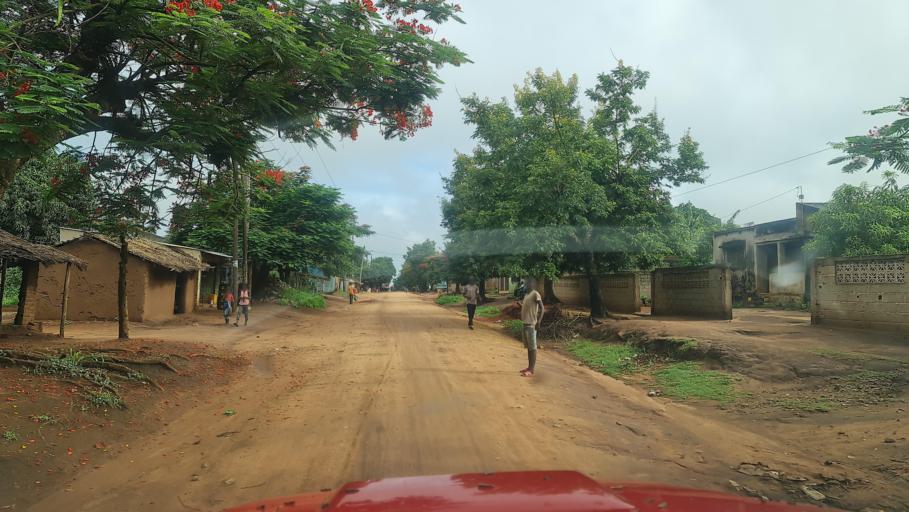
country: MW
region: Southern Region
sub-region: Nsanje District
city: Nsanje
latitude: -17.3234
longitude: 35.5917
